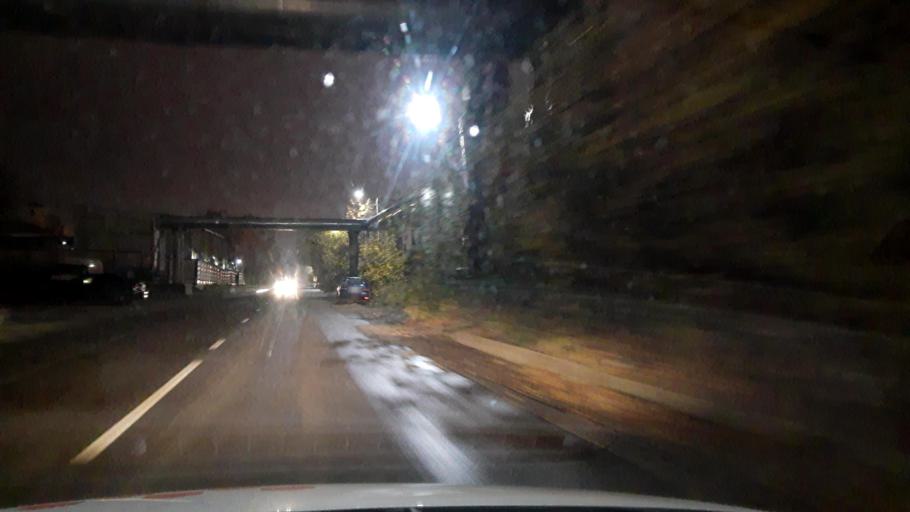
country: RU
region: Moskovskaya
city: Alekseyevka
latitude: 55.6339
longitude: 37.8122
